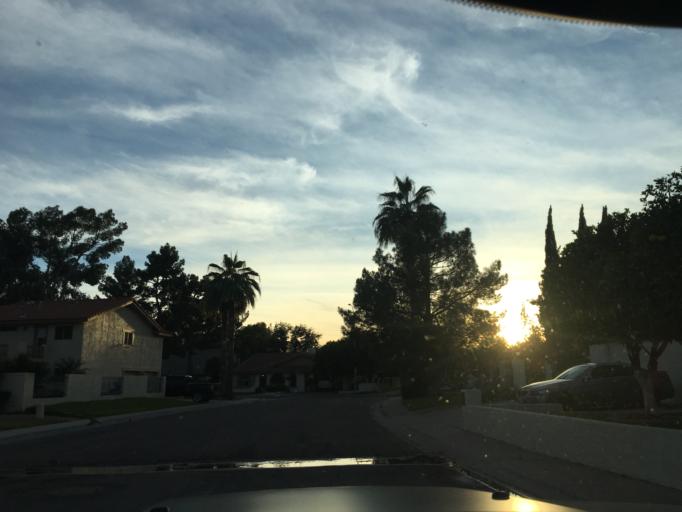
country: US
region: Arizona
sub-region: Maricopa County
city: Tempe
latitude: 33.3747
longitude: -111.9175
